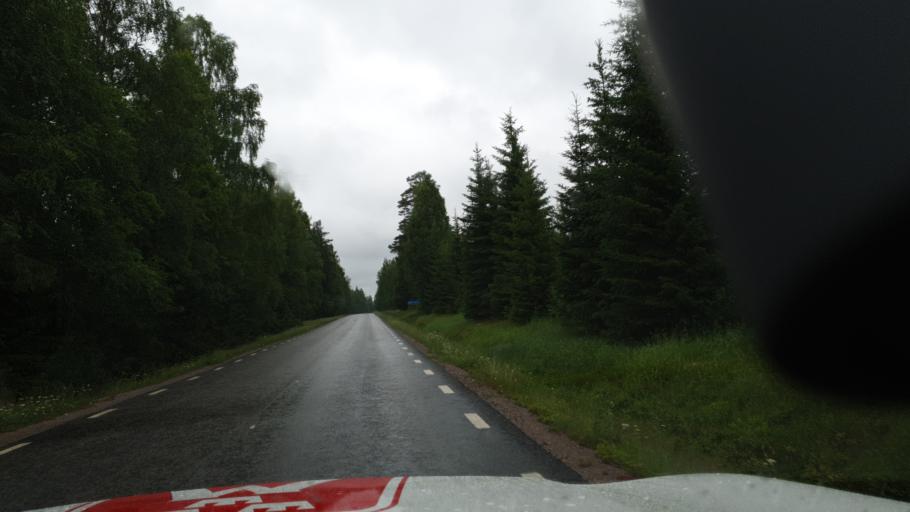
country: SE
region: Vaesterbotten
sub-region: Vannas Kommun
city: Vannasby
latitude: 63.8182
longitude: 19.8563
